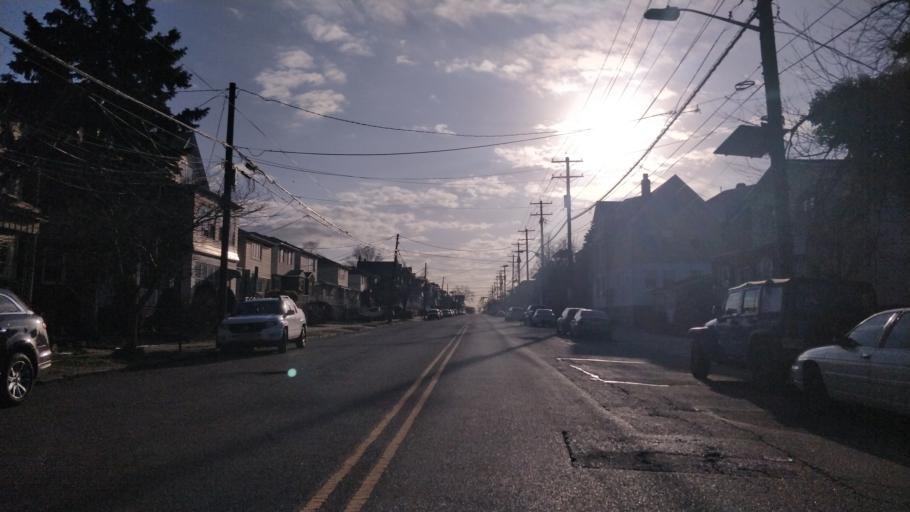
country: US
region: New Jersey
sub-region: Hudson County
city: Bayonne
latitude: 40.6716
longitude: -74.1085
